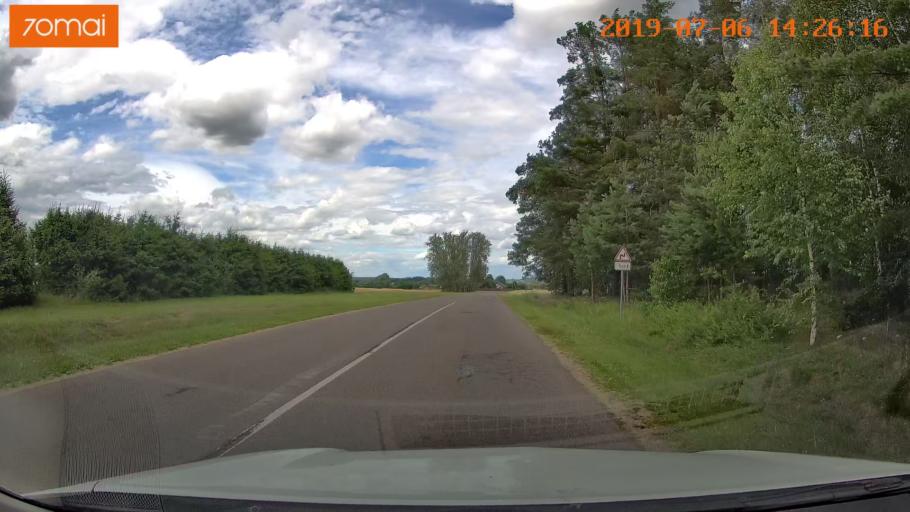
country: BY
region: Minsk
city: Ivyanyets
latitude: 53.9377
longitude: 26.7986
